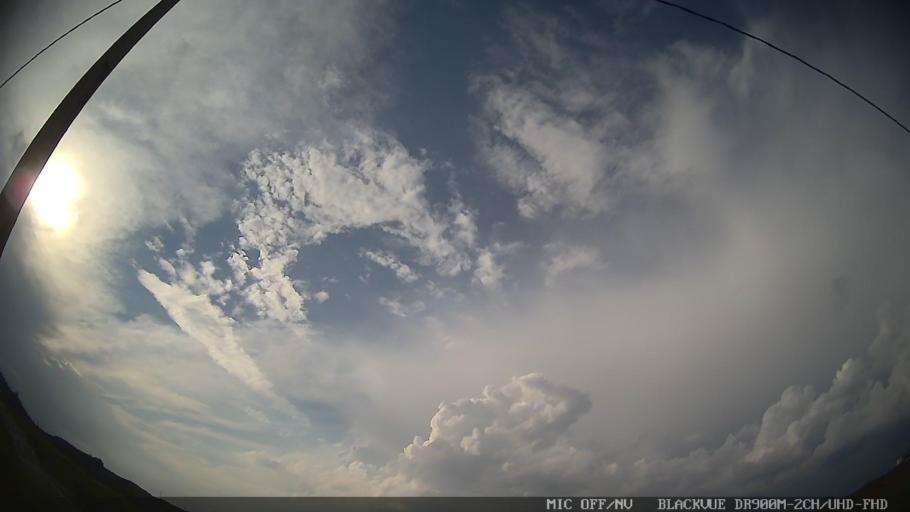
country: BR
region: Sao Paulo
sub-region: Braganca Paulista
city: Braganca Paulista
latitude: -22.9121
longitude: -46.5611
